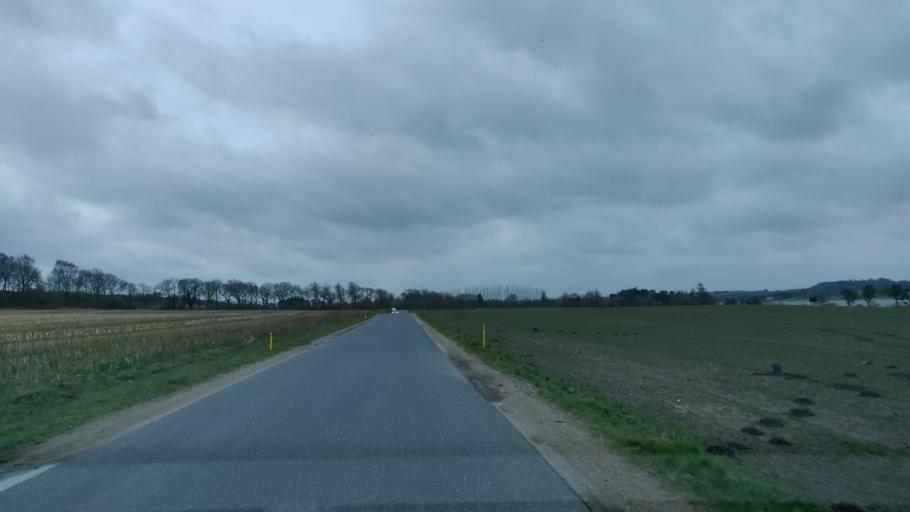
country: DK
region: Central Jutland
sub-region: Skive Kommune
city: Hojslev
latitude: 56.5504
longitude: 9.2420
